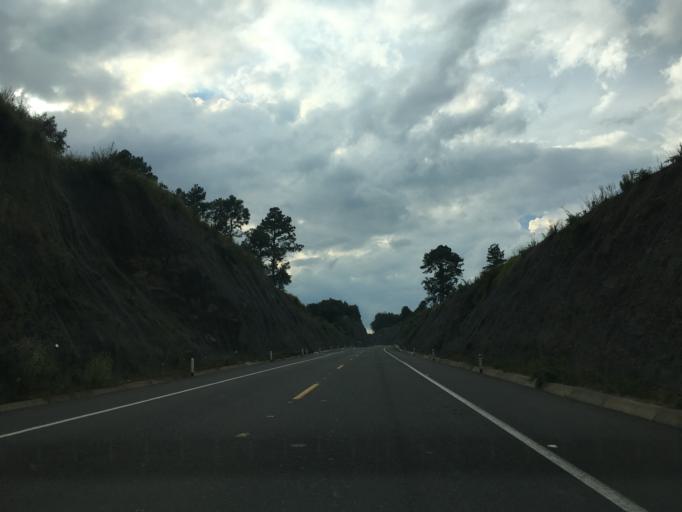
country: MX
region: Michoacan
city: Angahuan
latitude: 19.5075
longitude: -102.1524
